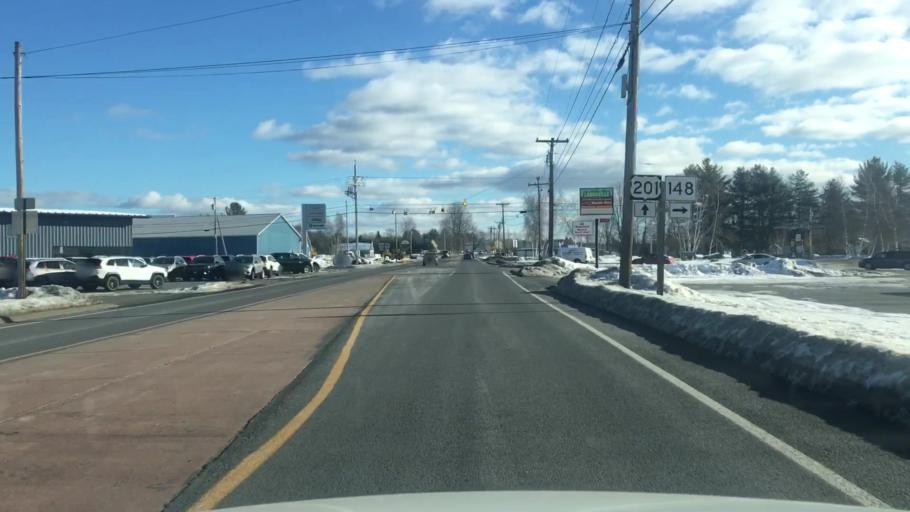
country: US
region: Maine
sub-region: Somerset County
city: Skowhegan
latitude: 44.8154
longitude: -69.7650
